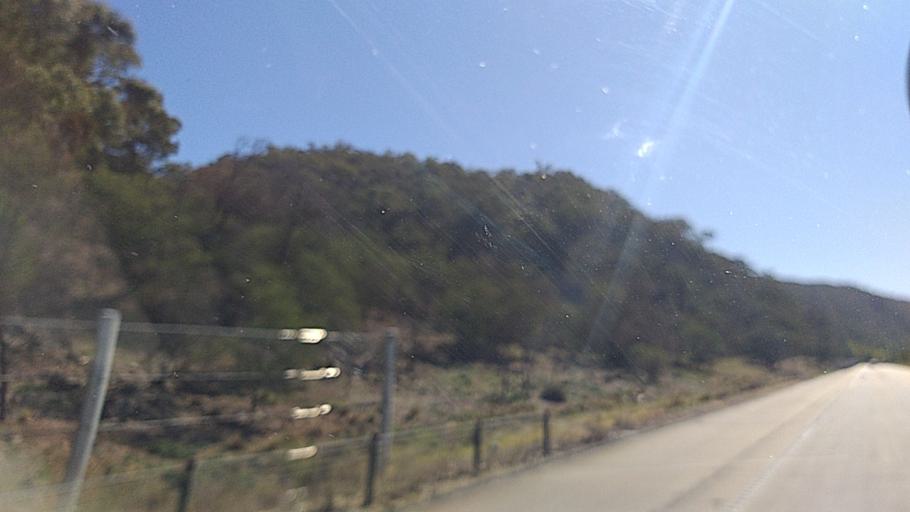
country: AU
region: New South Wales
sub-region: Yass Valley
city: Gundaroo
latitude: -35.0736
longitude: 149.3742
